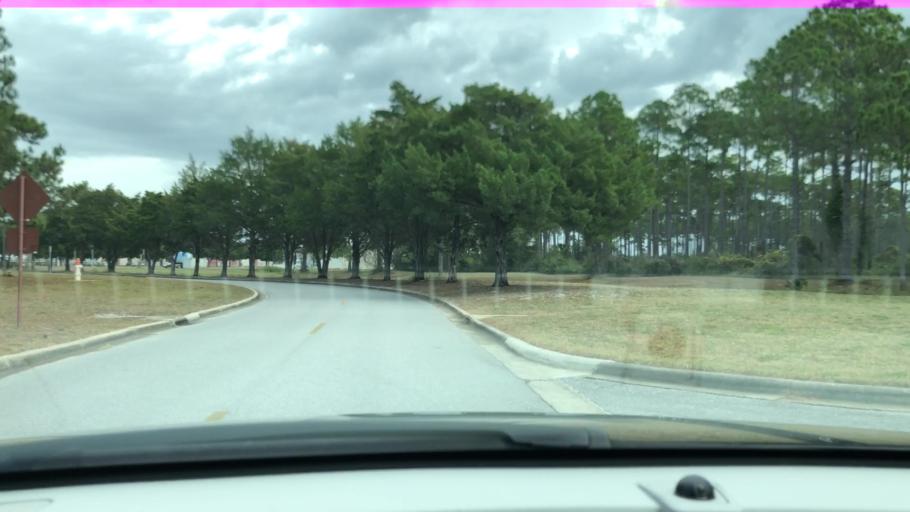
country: US
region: Florida
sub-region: Bay County
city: Tyndall Air Force Base
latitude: 30.0622
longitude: -85.5841
